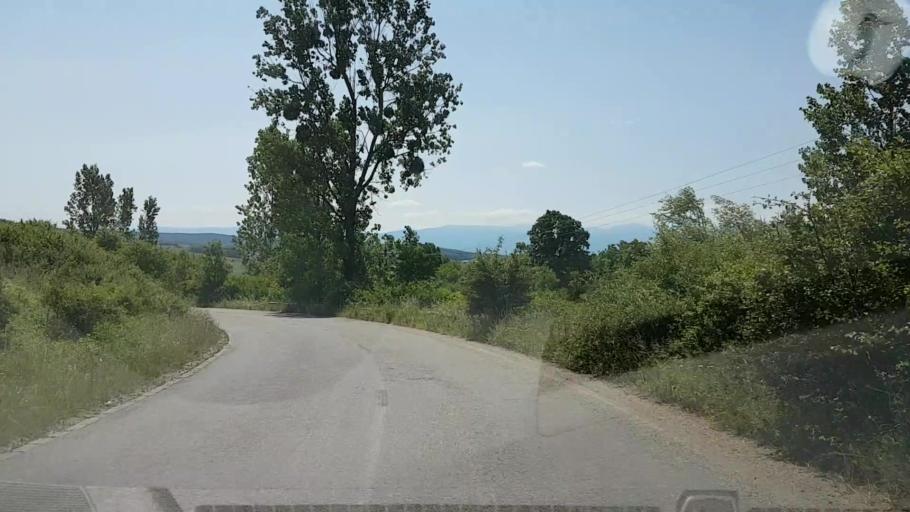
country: RO
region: Brasov
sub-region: Comuna Cincu
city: Cincu
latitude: 45.9342
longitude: 24.7903
